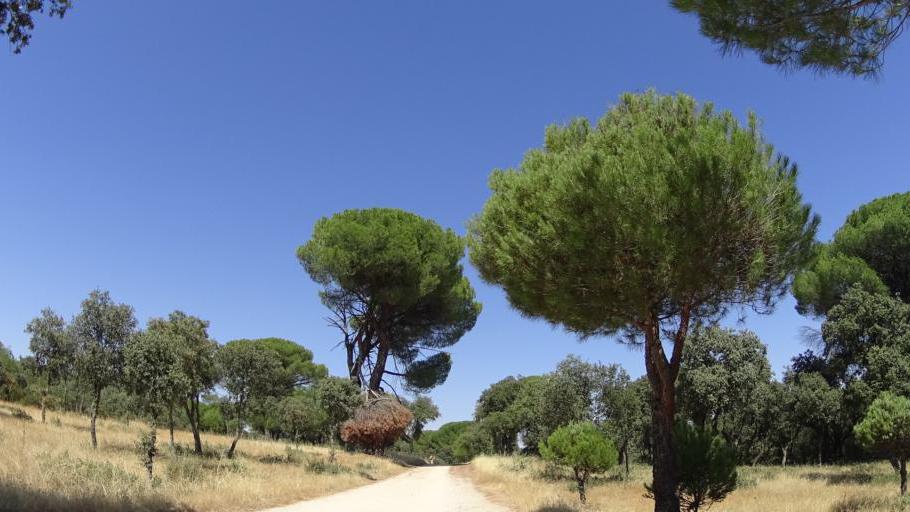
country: ES
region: Madrid
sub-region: Provincia de Madrid
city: Boadilla del Monte
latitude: 40.4373
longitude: -3.8613
